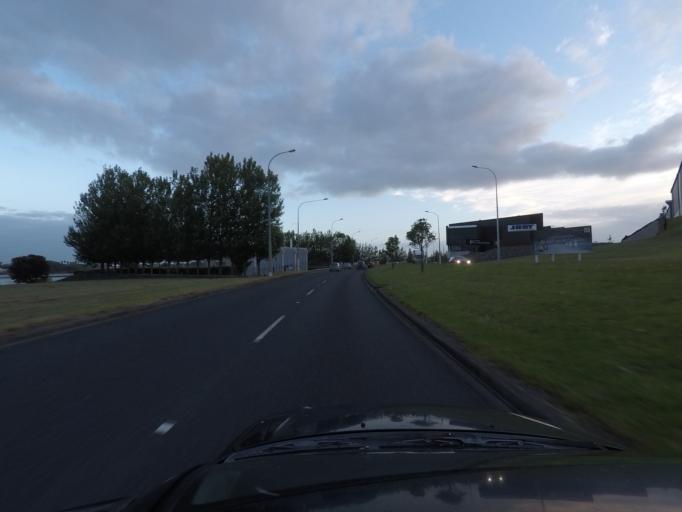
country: NZ
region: Auckland
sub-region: Auckland
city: Tamaki
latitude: -36.9414
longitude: 174.8632
